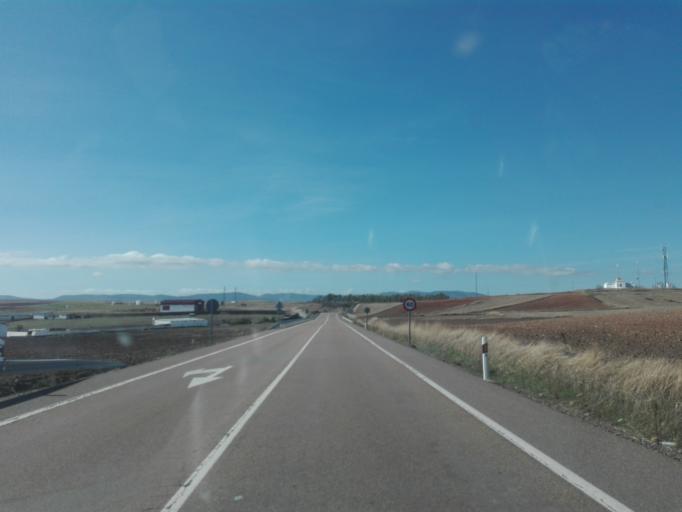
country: ES
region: Extremadura
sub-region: Provincia de Badajoz
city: Ahillones
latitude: 38.2622
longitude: -5.8673
